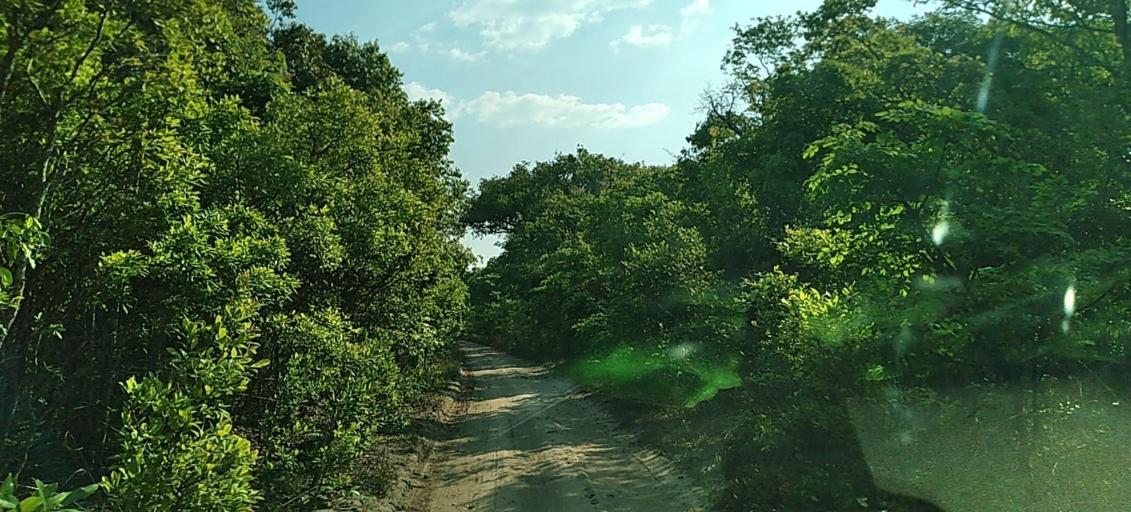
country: ZM
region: North-Western
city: Mwinilunga
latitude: -11.3167
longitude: 24.7408
